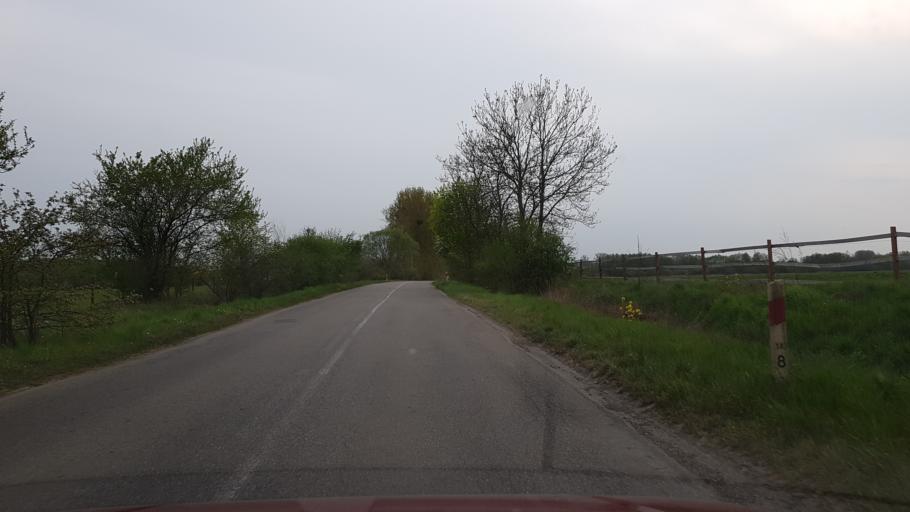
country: PL
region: West Pomeranian Voivodeship
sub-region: Powiat gryfinski
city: Stare Czarnowo
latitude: 53.2793
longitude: 14.7020
